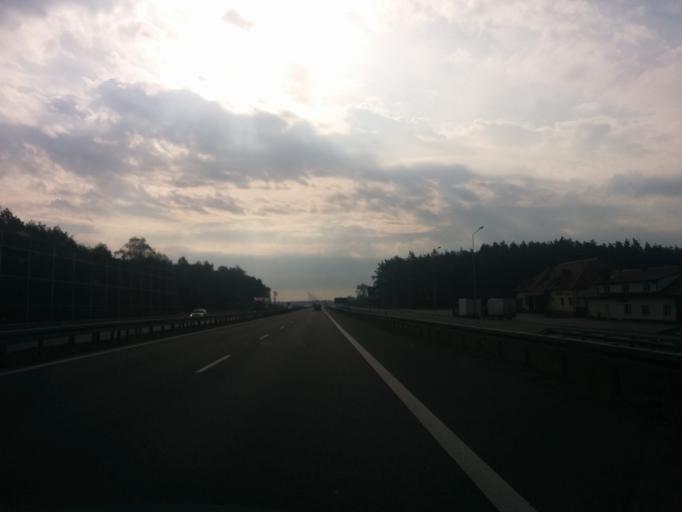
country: PL
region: Masovian Voivodeship
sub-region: Powiat bialobrzeski
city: Stara Blotnica
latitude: 51.5776
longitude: 21.0064
